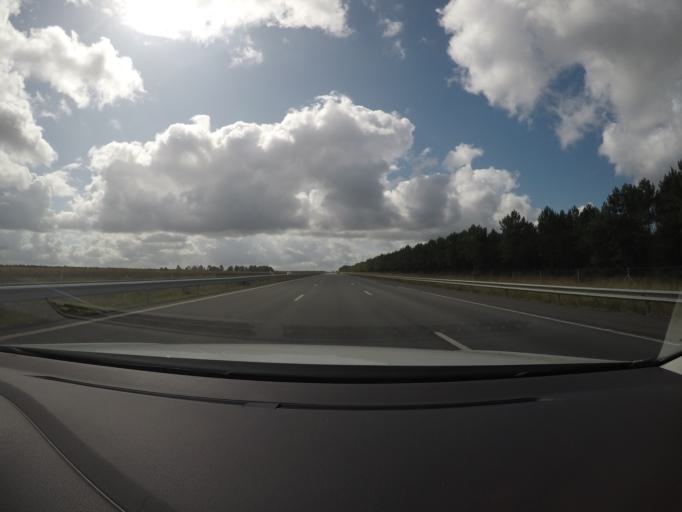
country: FR
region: Aquitaine
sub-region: Departement des Landes
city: Onesse-Laharie
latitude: 44.1185
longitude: -0.9865
